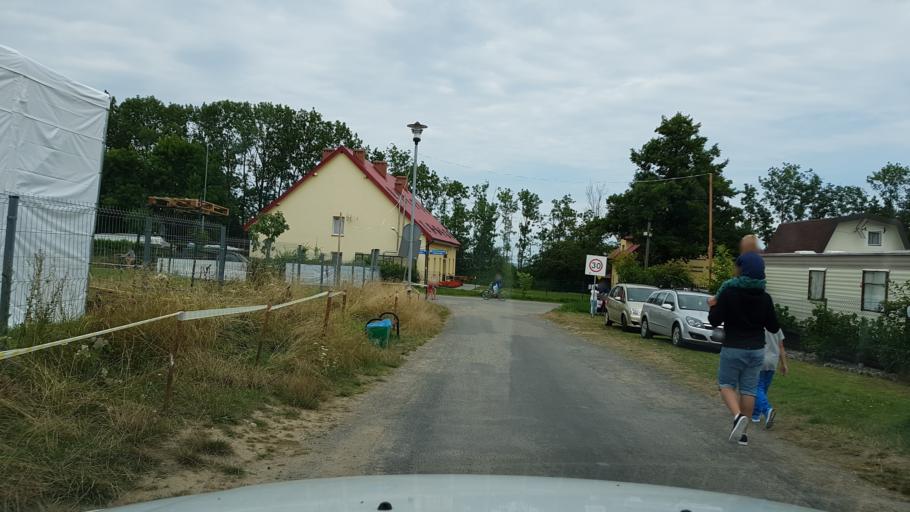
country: PL
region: West Pomeranian Voivodeship
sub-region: Powiat koszalinski
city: Mielno
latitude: 54.2461
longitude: 15.9334
